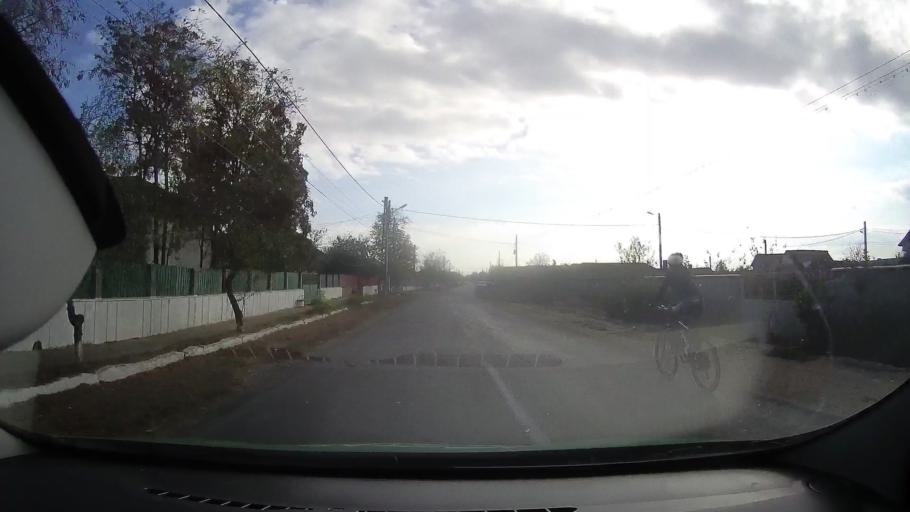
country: RO
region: Constanta
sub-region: Comuna Corbu
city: Corbu
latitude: 44.4196
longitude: 28.6608
